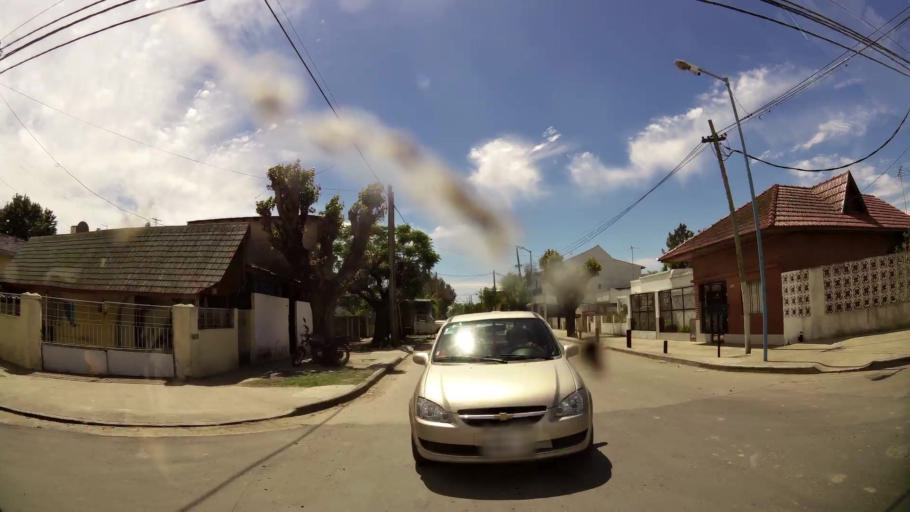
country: AR
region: Buenos Aires
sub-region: Partido de Quilmes
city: Quilmes
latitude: -34.7494
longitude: -58.2975
